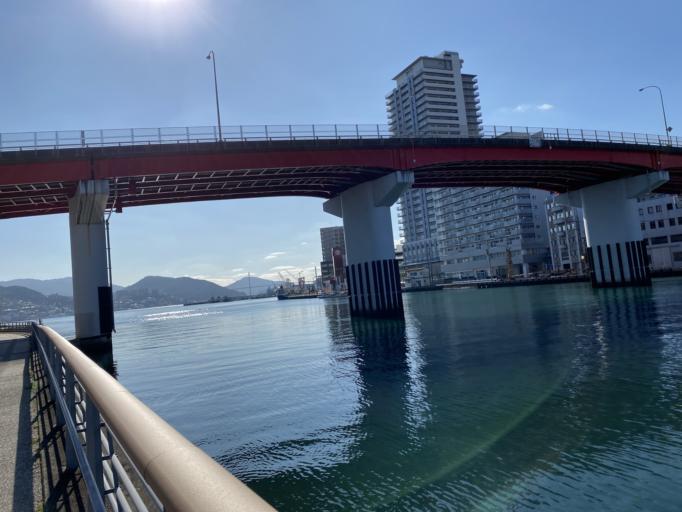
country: JP
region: Nagasaki
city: Nagasaki-shi
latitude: 32.7521
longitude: 129.8667
